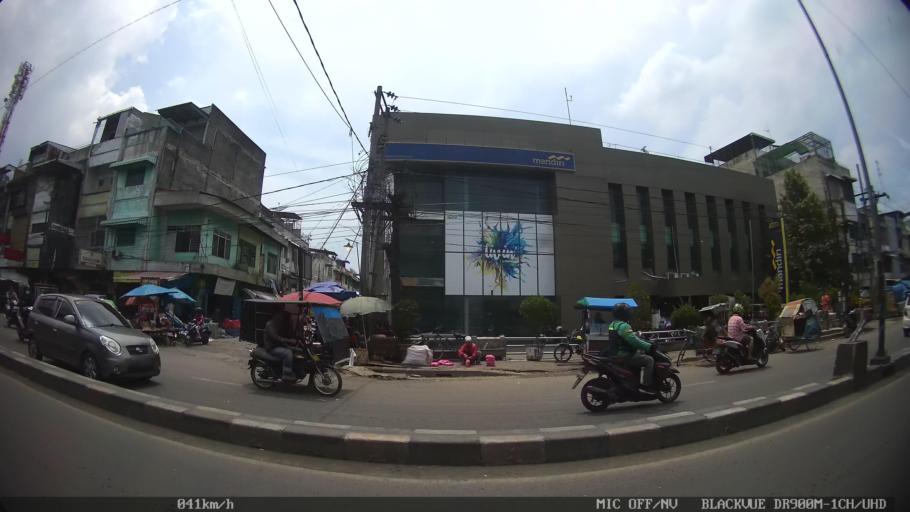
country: ID
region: North Sumatra
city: Medan
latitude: 3.6300
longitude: 98.6693
